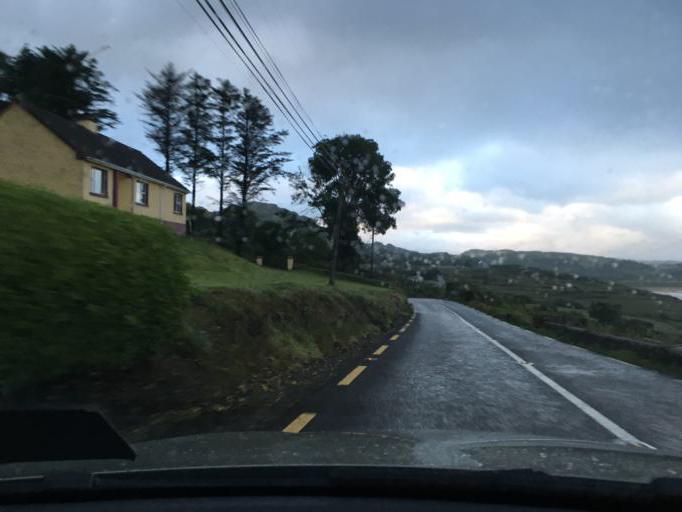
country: IE
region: Ulster
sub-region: County Donegal
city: Killybegs
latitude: 54.6323
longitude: -8.5052
